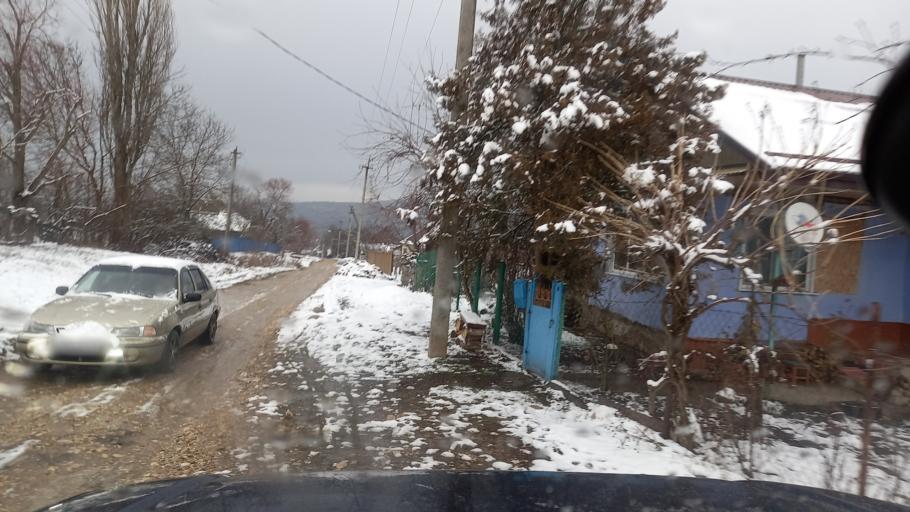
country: RU
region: Adygeya
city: Abadzekhskaya
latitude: 44.3579
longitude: 40.4105
